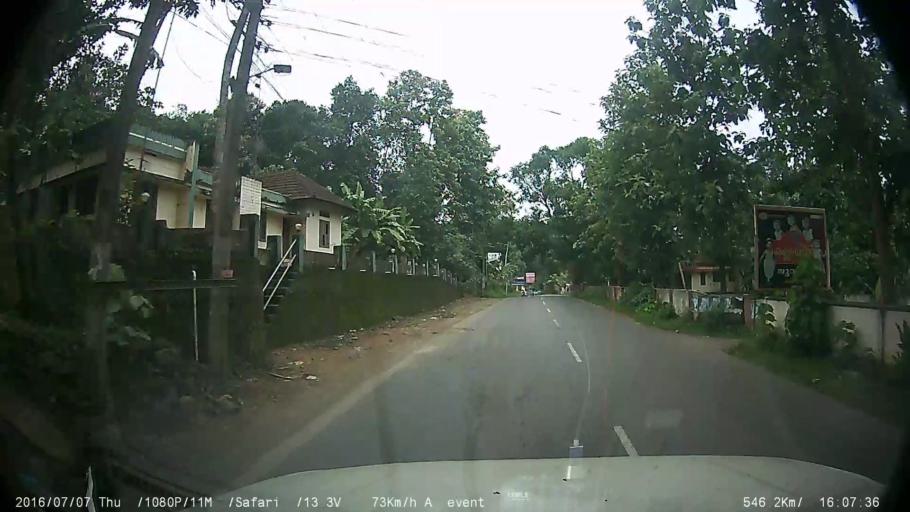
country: IN
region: Kerala
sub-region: Kottayam
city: Palackattumala
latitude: 9.8056
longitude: 76.6134
